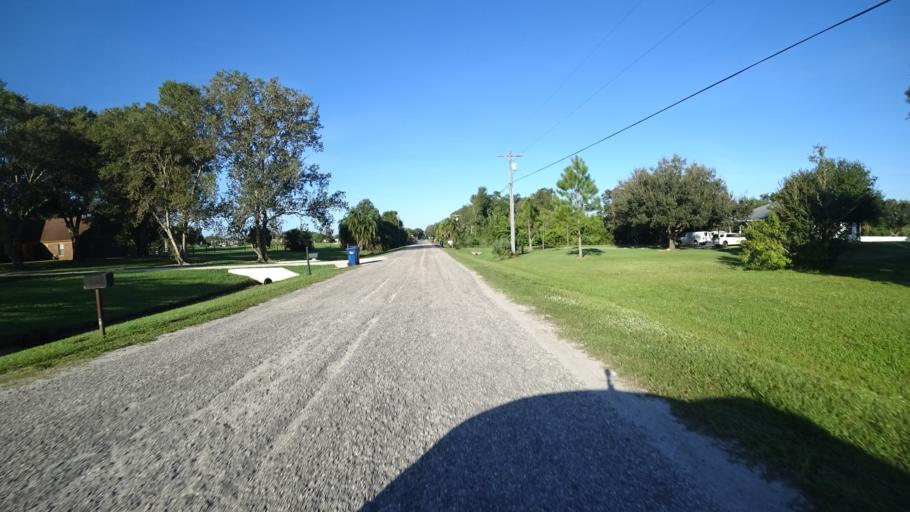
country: US
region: Florida
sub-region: Manatee County
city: Ellenton
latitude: 27.5682
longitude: -82.5250
